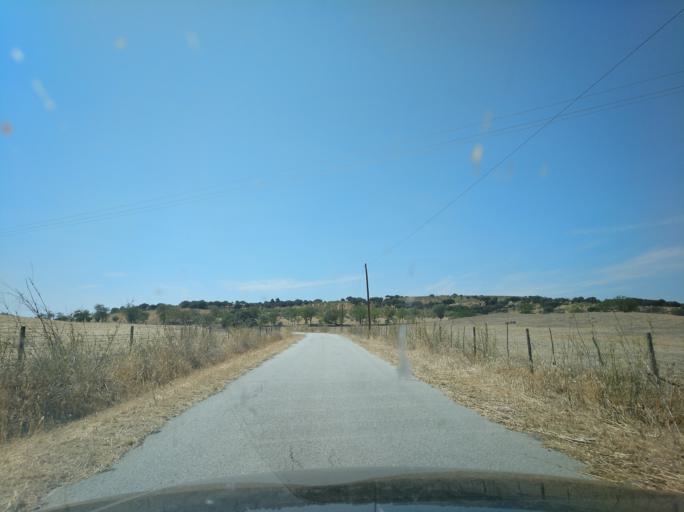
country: PT
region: Portalegre
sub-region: Campo Maior
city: Campo Maior
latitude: 38.9616
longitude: -7.1197
